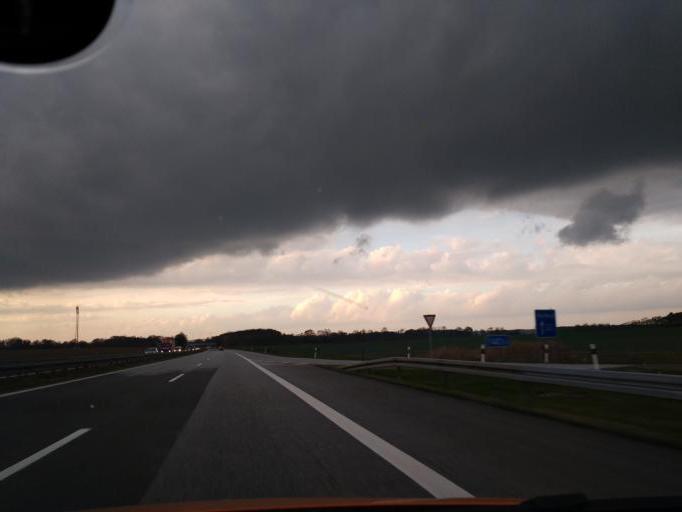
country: DE
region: Brandenburg
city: Gerdshagen
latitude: 53.2642
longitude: 12.1429
